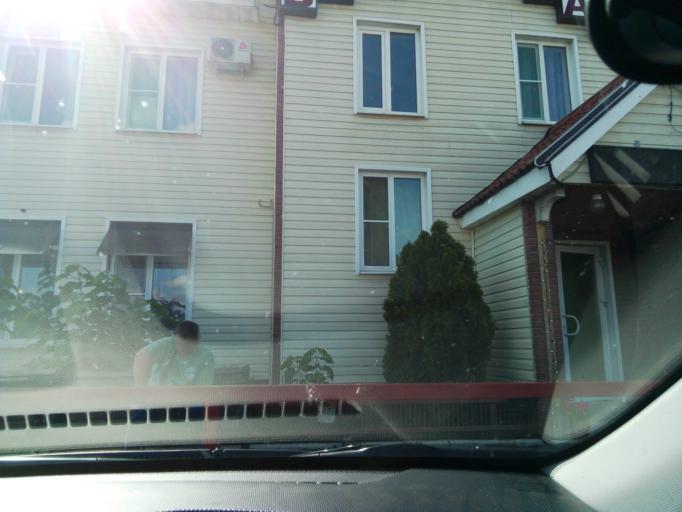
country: RU
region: Voronezj
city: Losevo
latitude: 50.6897
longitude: 40.0575
